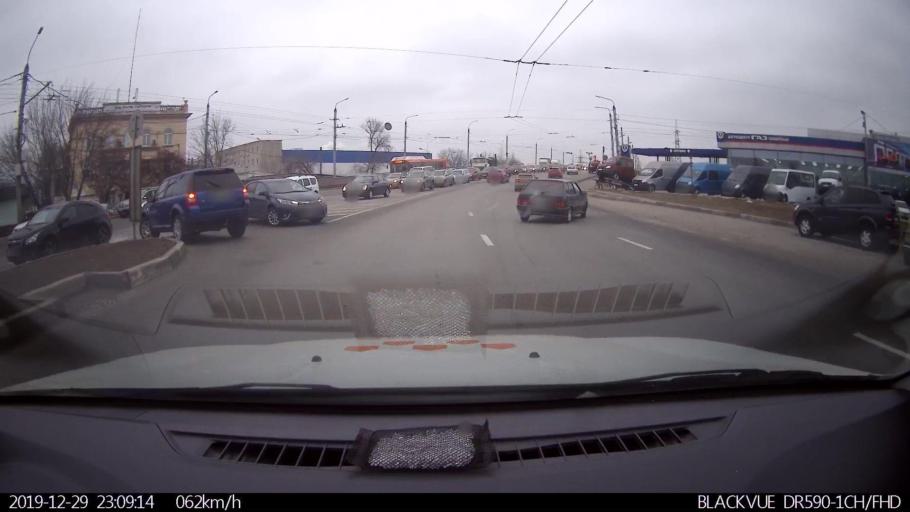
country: RU
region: Nizjnij Novgorod
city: Nizhniy Novgorod
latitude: 56.2583
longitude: 43.9044
